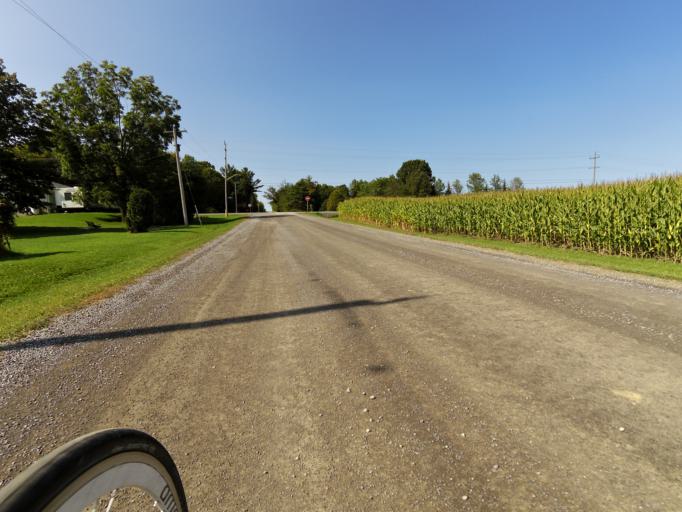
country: CA
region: Ontario
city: Arnprior
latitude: 45.3993
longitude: -76.1751
